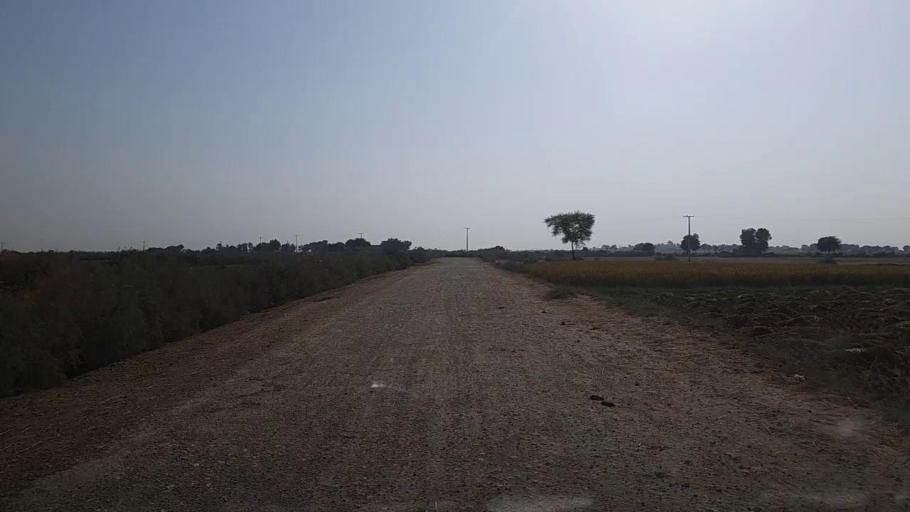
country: PK
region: Sindh
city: Kandhkot
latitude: 28.3842
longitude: 69.3363
